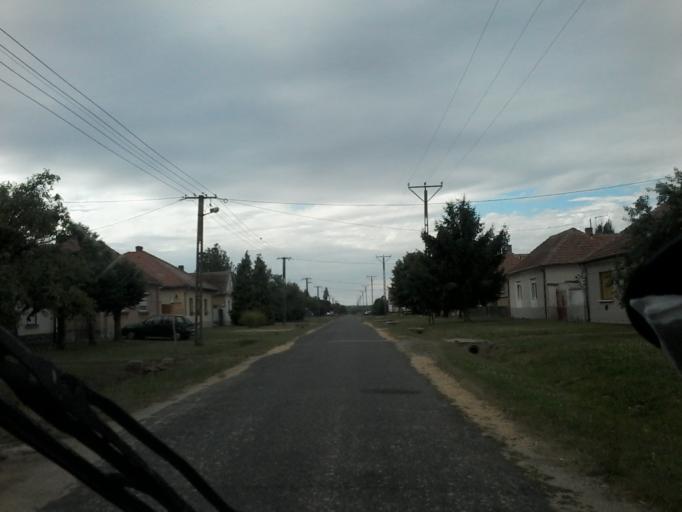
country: HU
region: Vas
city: Celldomolk
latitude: 47.2085
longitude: 17.0597
